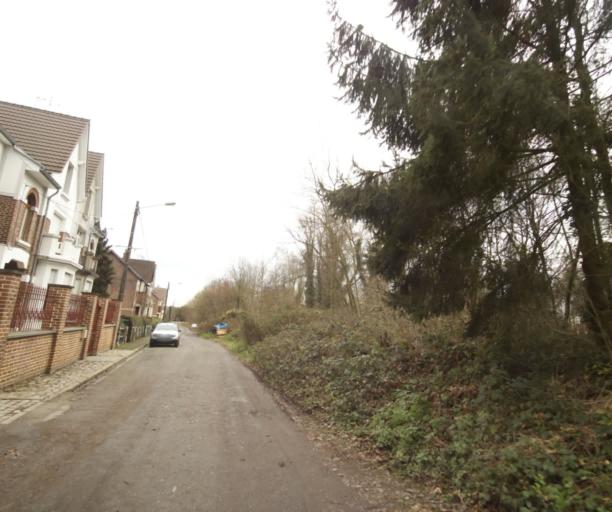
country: FR
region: Nord-Pas-de-Calais
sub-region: Departement du Nord
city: Vieux-Conde
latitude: 50.4513
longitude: 3.5564
